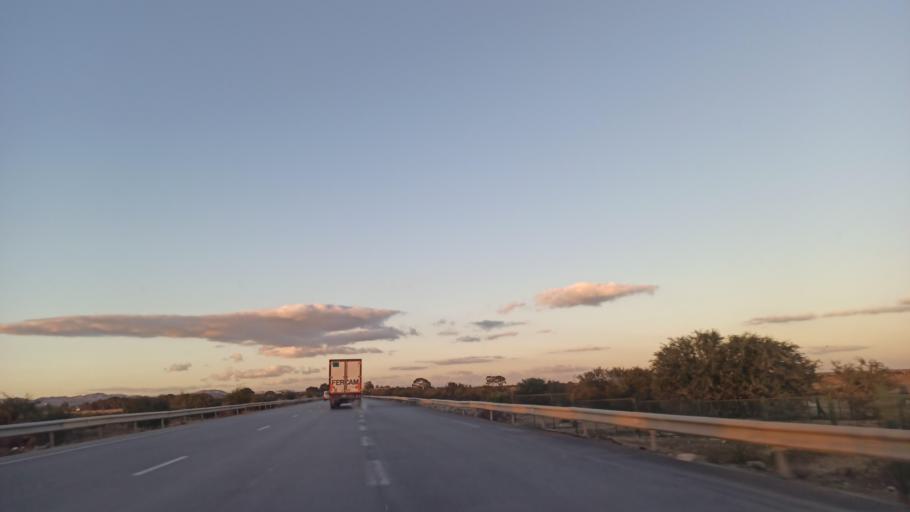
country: TN
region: Susah
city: Harqalah
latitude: 36.1118
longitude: 10.4049
